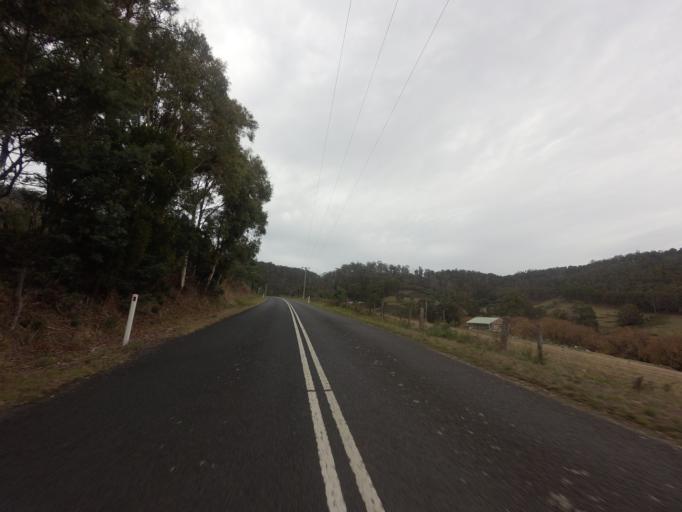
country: AU
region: Tasmania
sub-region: Derwent Valley
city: New Norfolk
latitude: -42.5927
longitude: 147.0368
